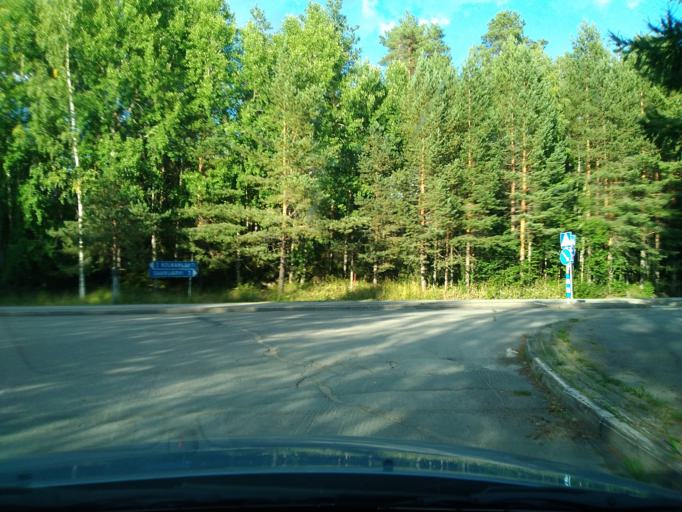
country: FI
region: Central Finland
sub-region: Saarijaervi-Viitasaari
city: Saarijaervi
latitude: 62.7104
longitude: 25.2135
